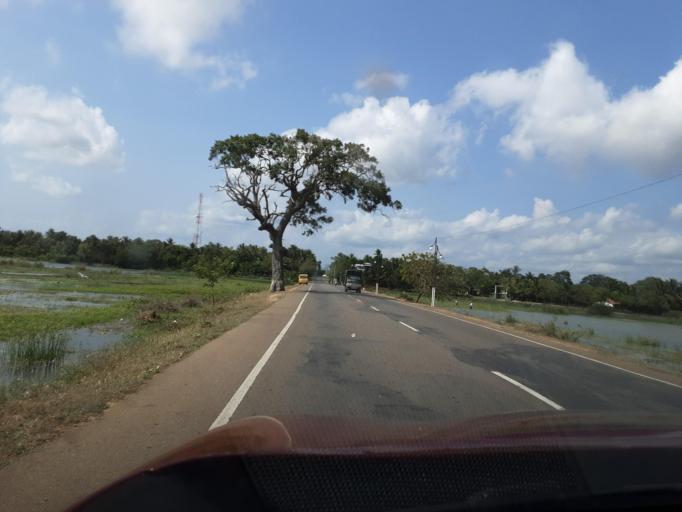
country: LK
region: Southern
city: Tangalla
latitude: 6.2924
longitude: 81.2352
